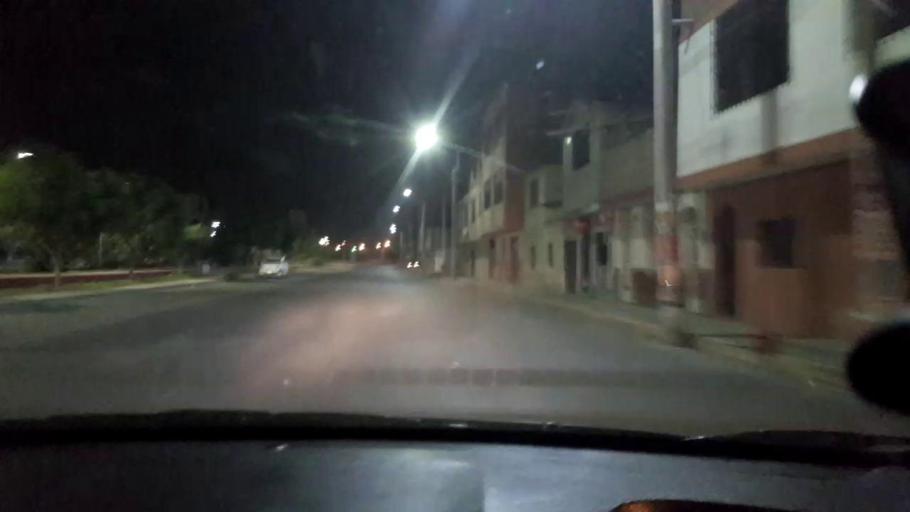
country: PE
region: Lambayeque
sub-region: Provincia de Chiclayo
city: Chiclayo
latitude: -6.7850
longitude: -79.8356
